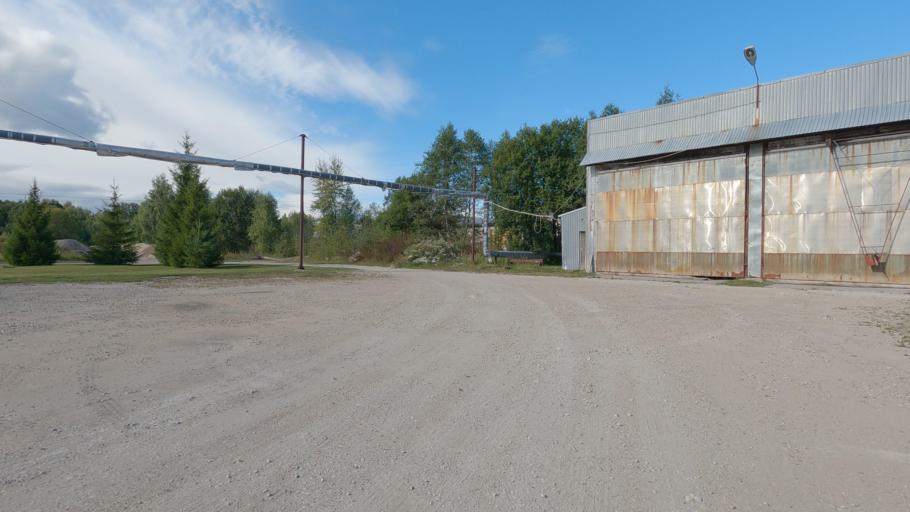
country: EE
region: Raplamaa
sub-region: Rapla vald
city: Rapla
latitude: 58.9963
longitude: 24.8278
